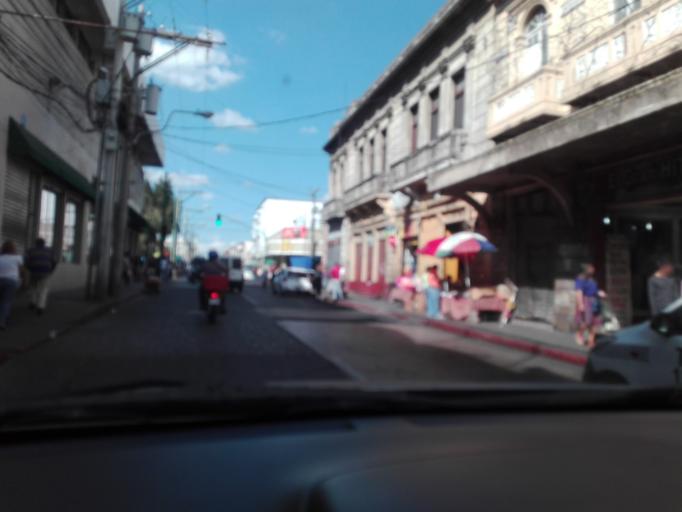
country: GT
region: Guatemala
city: Guatemala City
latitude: 14.6404
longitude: -90.5109
